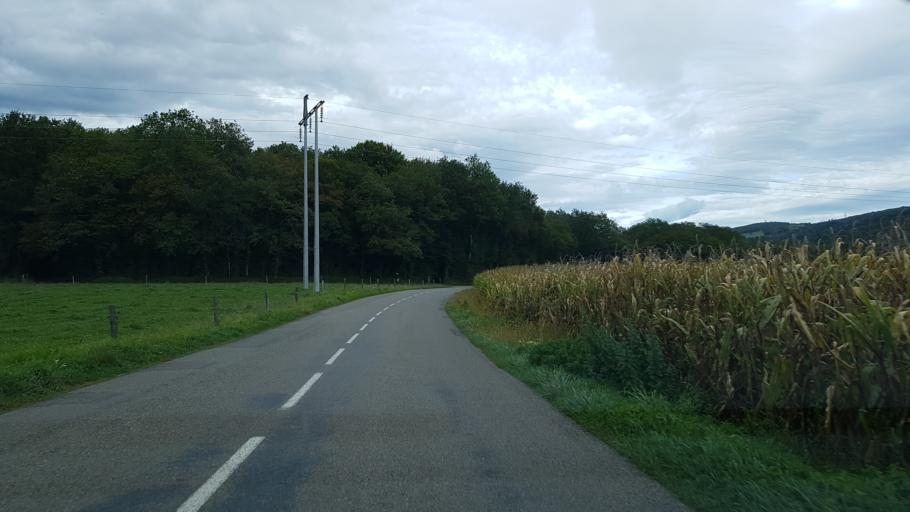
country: FR
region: Rhone-Alpes
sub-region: Departement de l'Ain
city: Villereversure
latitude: 46.2056
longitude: 5.4008
